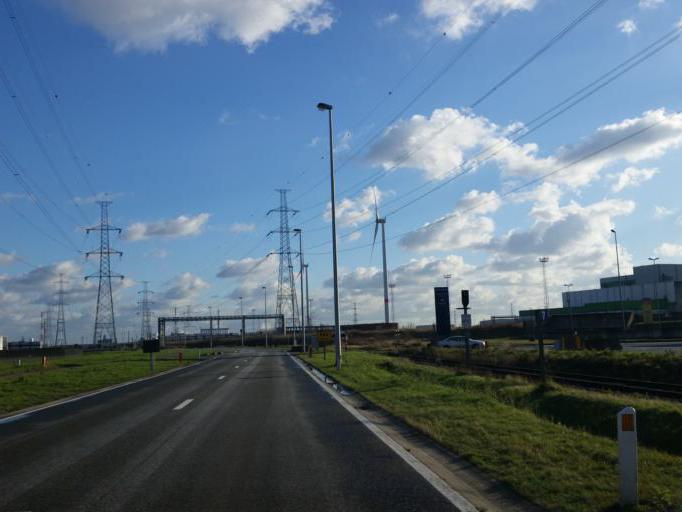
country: BE
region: Flanders
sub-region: Provincie Oost-Vlaanderen
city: Beveren
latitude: 51.2913
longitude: 4.2711
